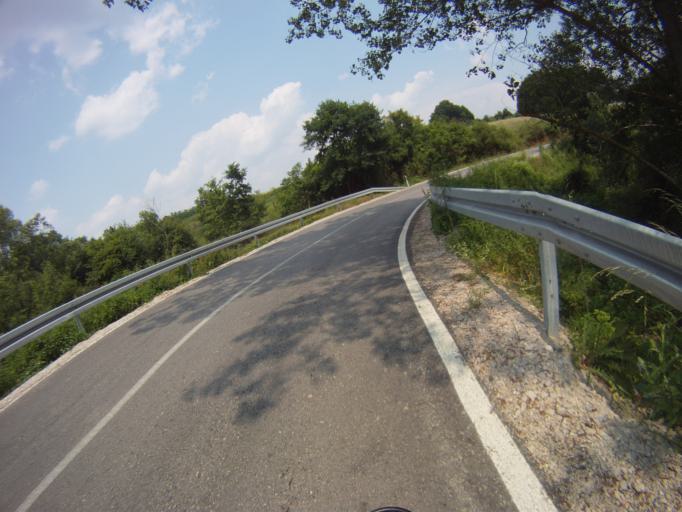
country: RS
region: Central Serbia
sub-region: Nisavski Okrug
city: Gadzin Han
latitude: 43.2081
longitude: 22.0134
